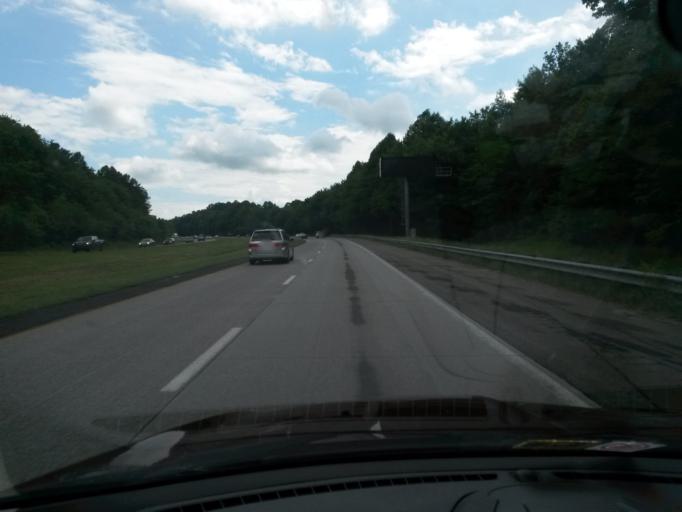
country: US
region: Virginia
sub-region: Carroll County
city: Cana
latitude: 36.5400
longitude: -80.7499
